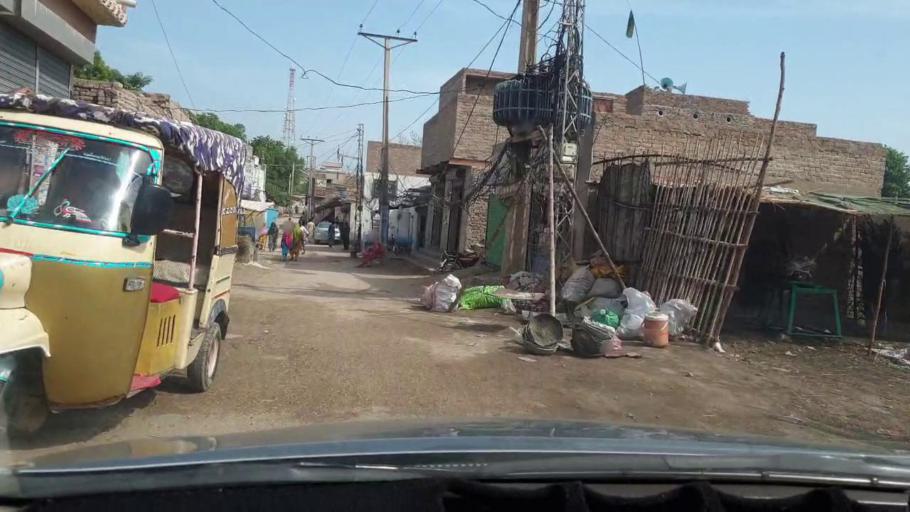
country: PK
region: Sindh
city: Khairpur
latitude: 27.5360
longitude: 68.7522
